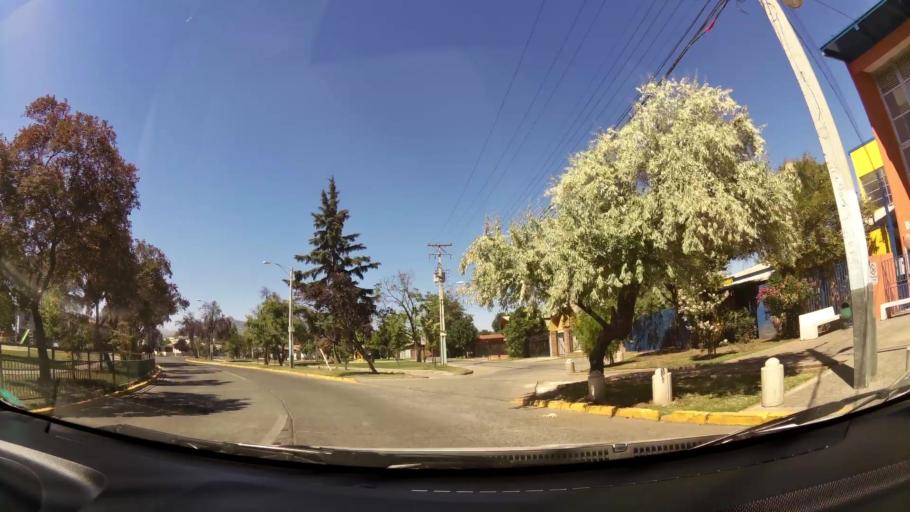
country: CL
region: O'Higgins
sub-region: Provincia de Cachapoal
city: Rancagua
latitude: -34.1677
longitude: -70.7304
